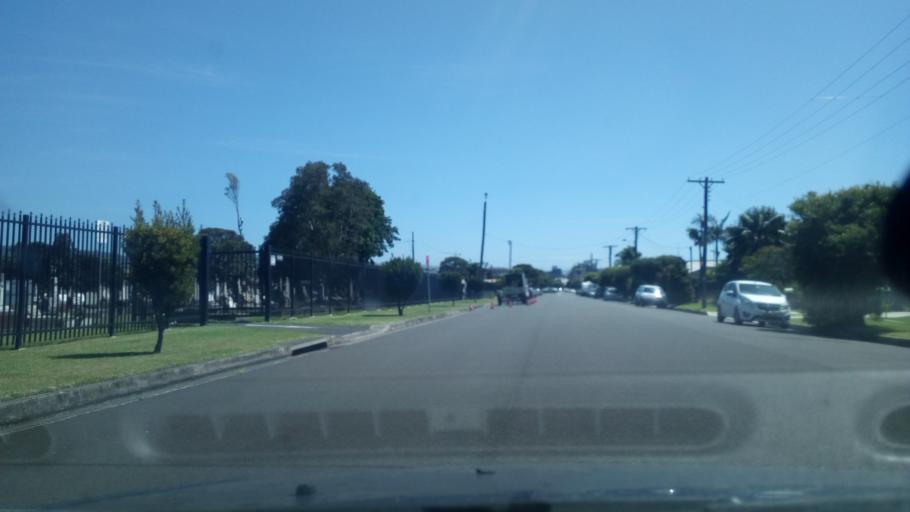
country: AU
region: New South Wales
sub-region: Wollongong
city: Wollongong
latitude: -34.4370
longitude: 150.8904
